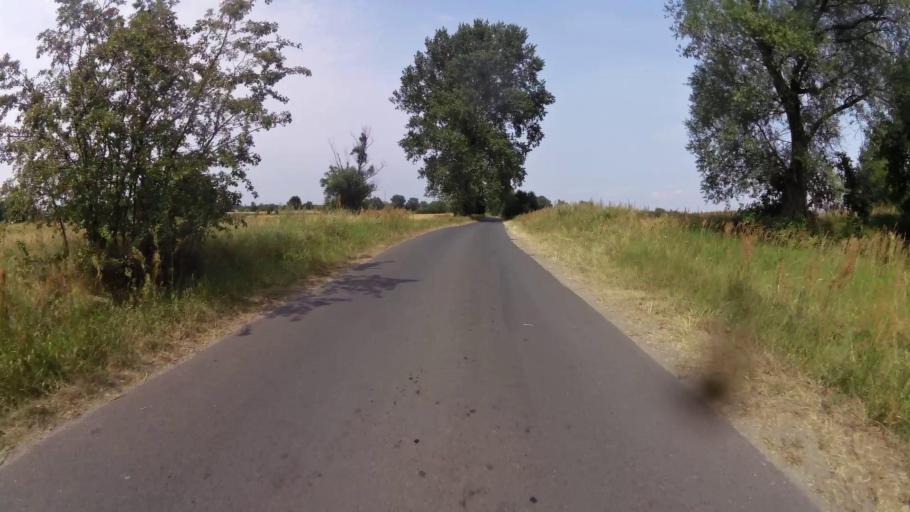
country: PL
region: West Pomeranian Voivodeship
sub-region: Powiat mysliborski
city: Nowogrodek Pomorski
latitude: 52.9686
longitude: 15.0221
